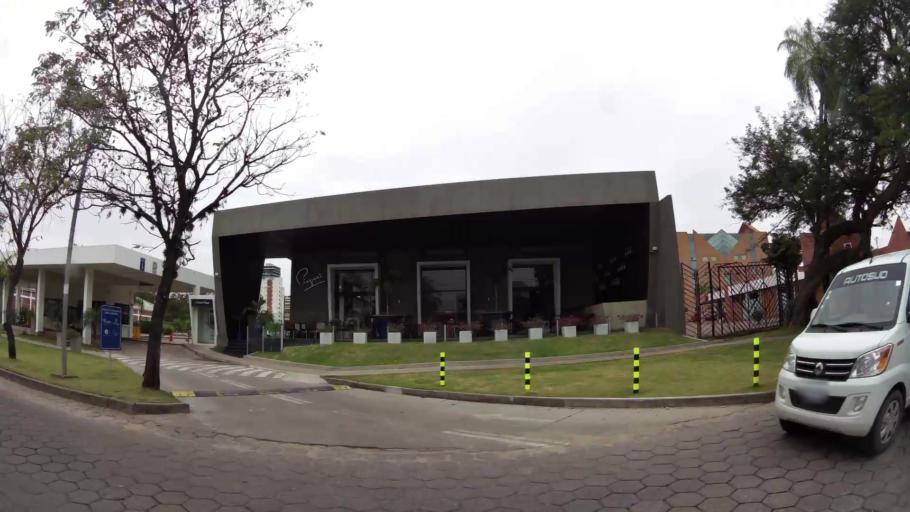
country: BO
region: Santa Cruz
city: Santa Cruz de la Sierra
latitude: -17.7652
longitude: -63.1996
